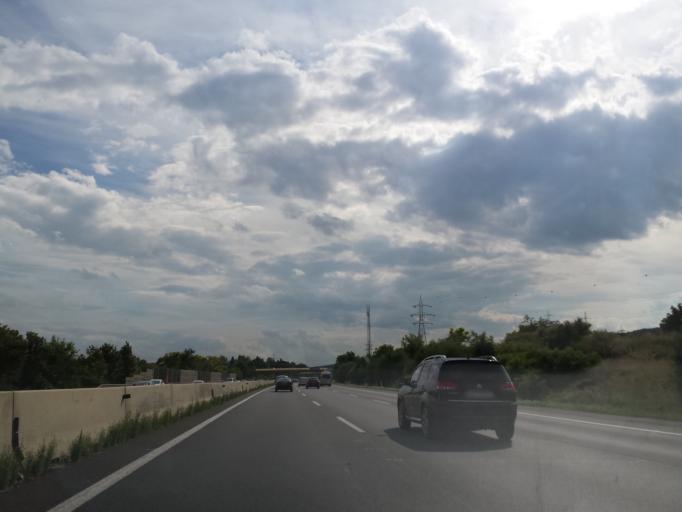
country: AT
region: Lower Austria
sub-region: Politischer Bezirk Wiener Neustadt
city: Felixdorf
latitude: 47.8780
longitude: 16.2019
